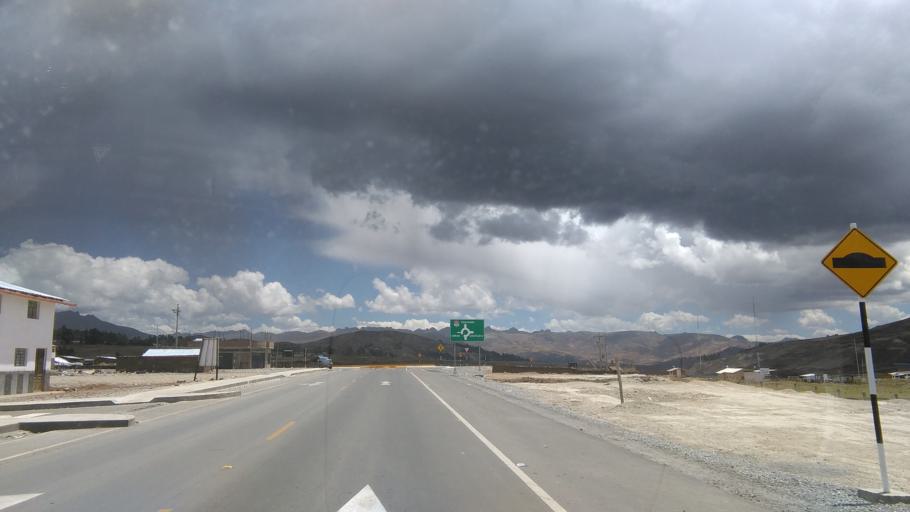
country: PE
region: Apurimac
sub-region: Provincia de Andahuaylas
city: San Jeronimo
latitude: -13.7120
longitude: -73.3498
